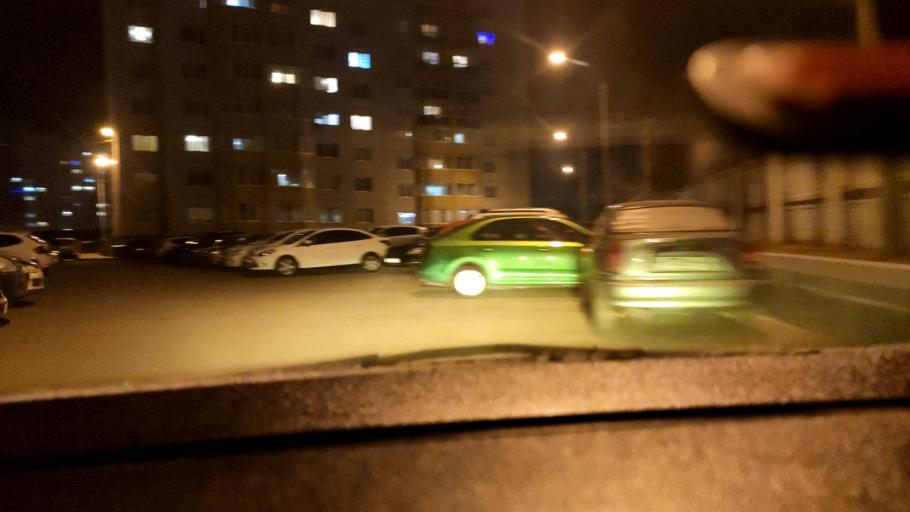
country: RU
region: Voronezj
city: Podgornoye
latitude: 51.7195
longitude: 39.1410
